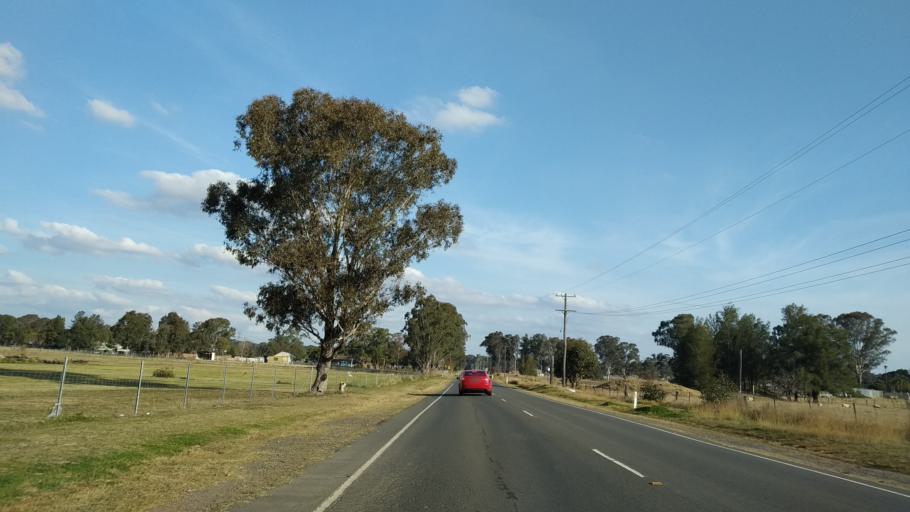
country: AU
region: New South Wales
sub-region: Penrith Municipality
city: Werrington County
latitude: -33.7056
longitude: 150.7574
